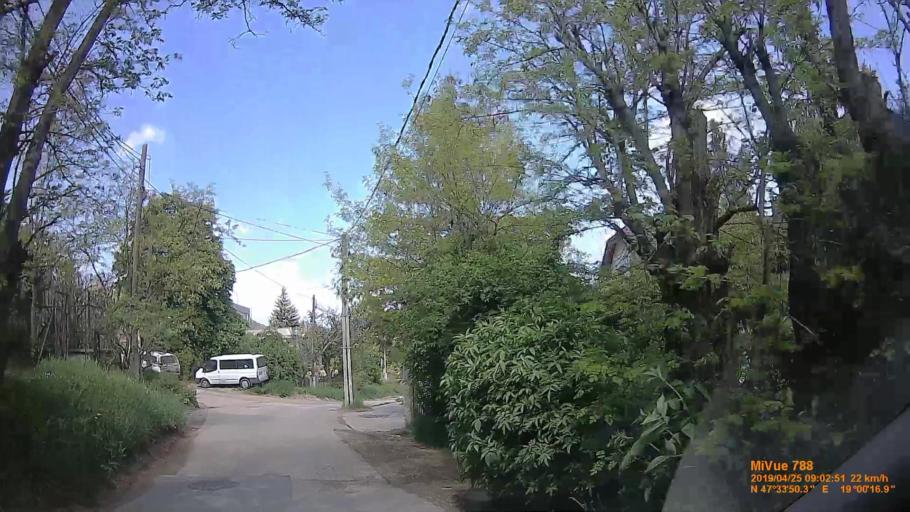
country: HU
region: Pest
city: Urom
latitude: 47.5640
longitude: 19.0046
